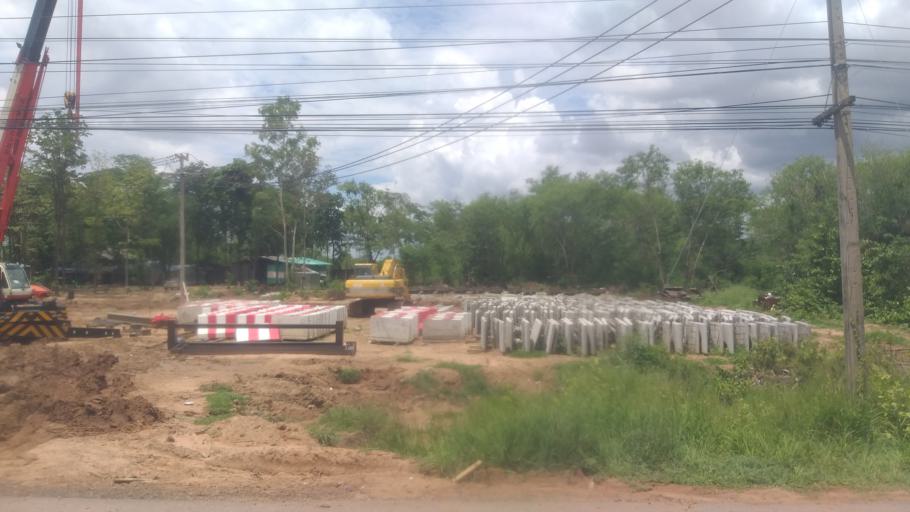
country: TH
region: Nakhon Ratchasima
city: Non Thai
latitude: 15.0967
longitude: 102.1070
